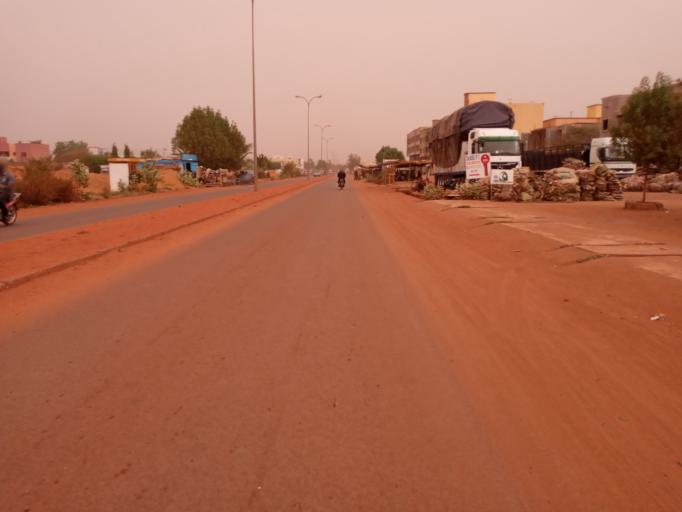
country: ML
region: Bamako
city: Bamako
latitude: 12.6520
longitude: -7.9345
